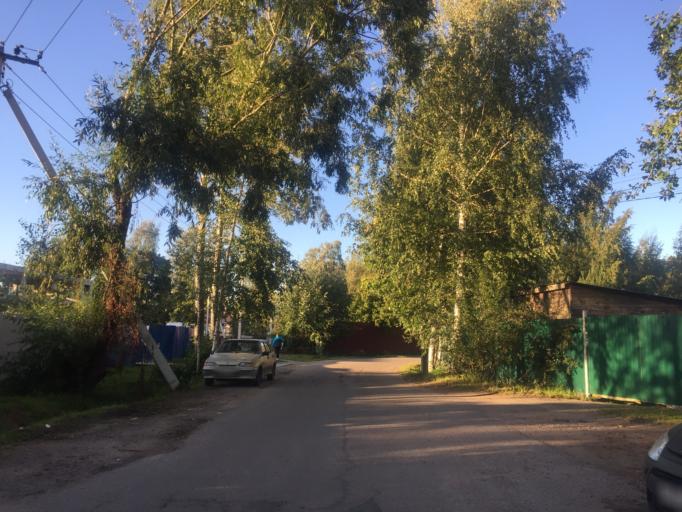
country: RU
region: Leningrad
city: Murino
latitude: 60.0441
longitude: 30.4422
